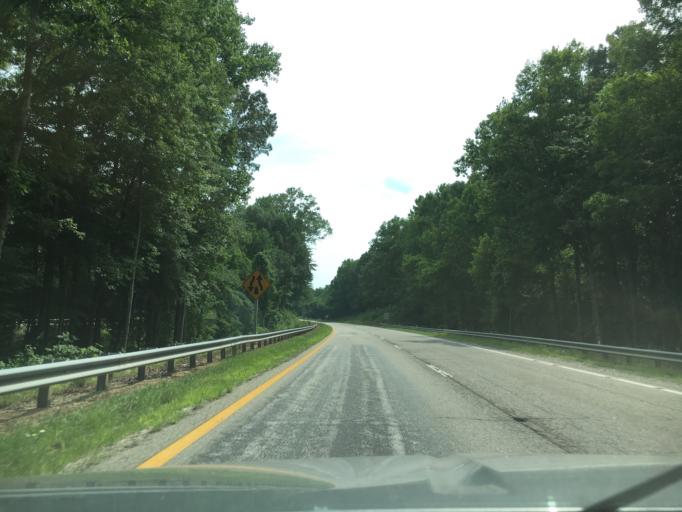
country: US
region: Virginia
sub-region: Lunenburg County
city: Victoria
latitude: 37.1412
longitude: -78.3052
